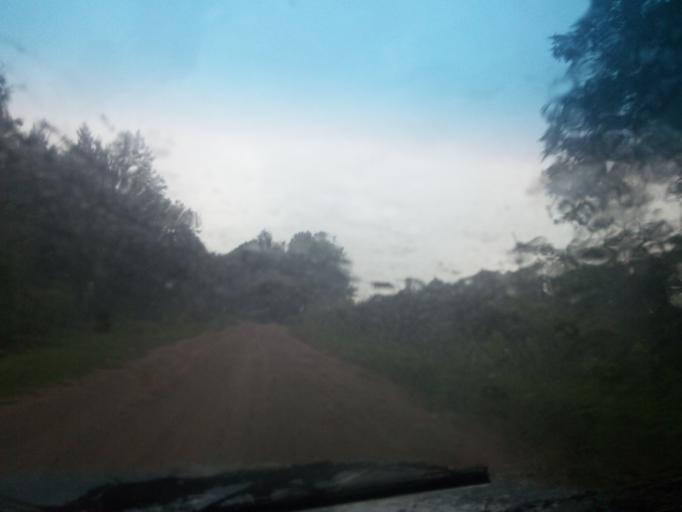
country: BY
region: Vitebsk
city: Dzisna
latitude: 55.6739
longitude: 28.3136
